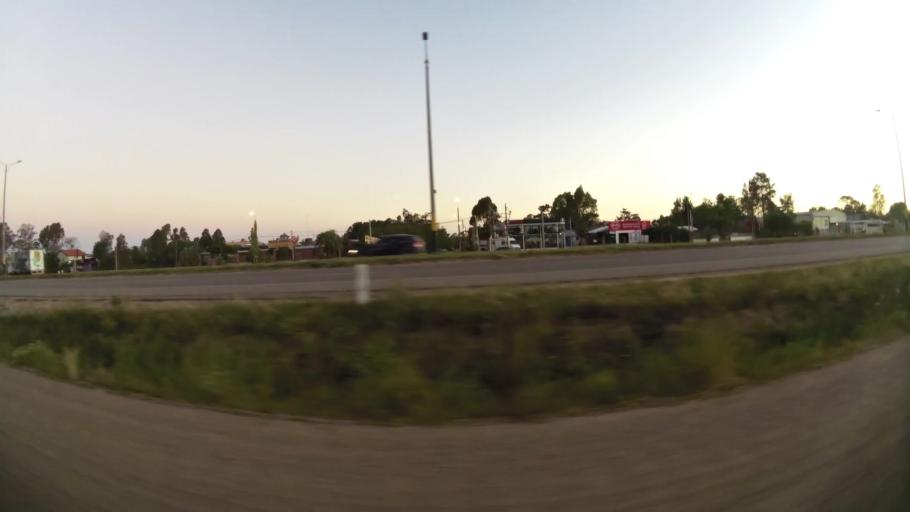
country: UY
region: Canelones
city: Colonia Nicolich
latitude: -34.8185
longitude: -55.9525
